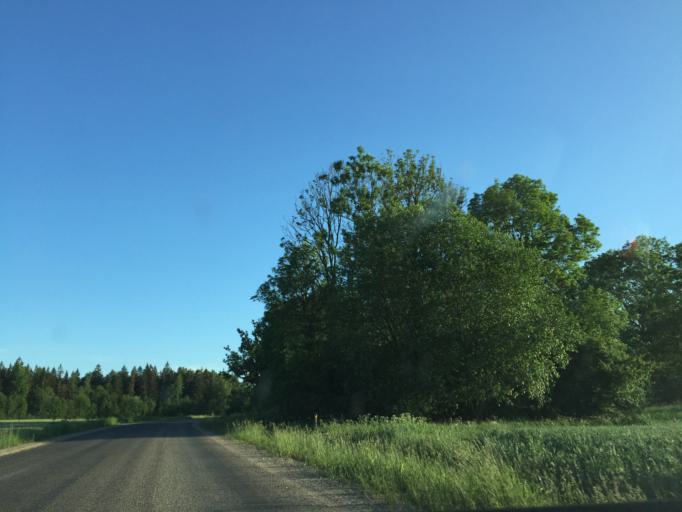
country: LV
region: Broceni
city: Broceni
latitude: 56.7354
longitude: 22.5075
